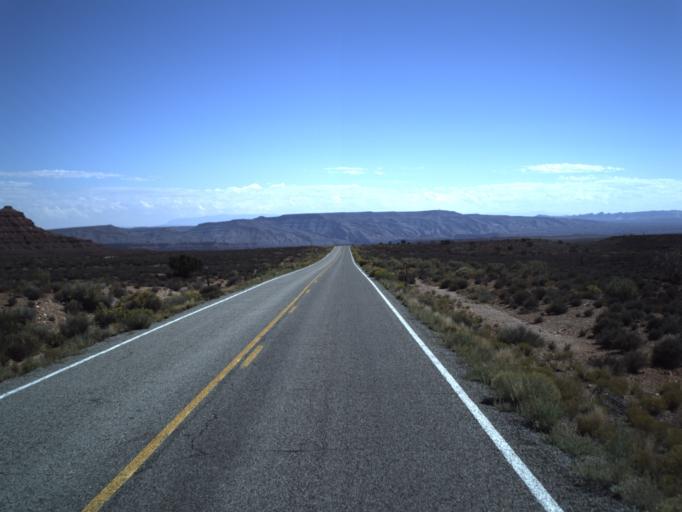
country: US
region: Utah
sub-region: San Juan County
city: Blanding
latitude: 37.2480
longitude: -109.9197
